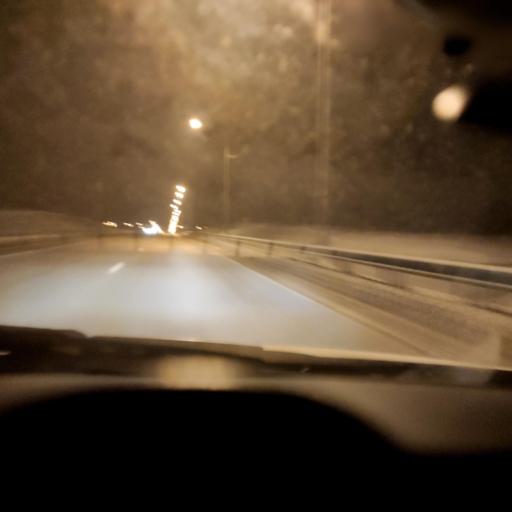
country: RU
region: Kursk
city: Fatezh
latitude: 52.0921
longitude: 35.8193
